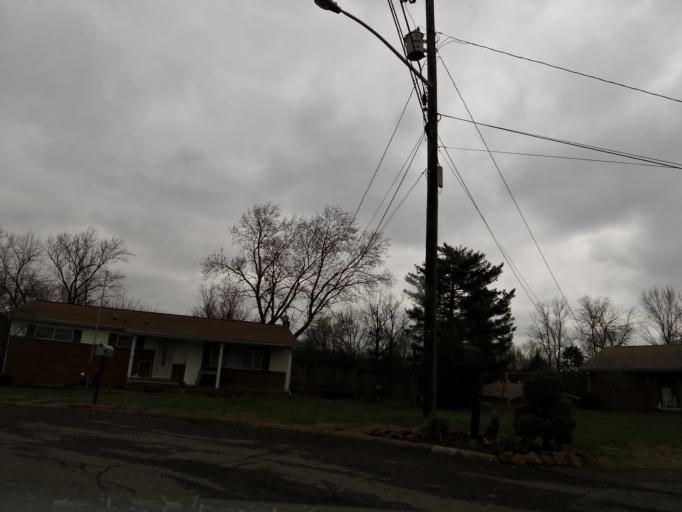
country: US
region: Tennessee
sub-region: Knox County
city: Knoxville
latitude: 35.9806
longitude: -84.0067
